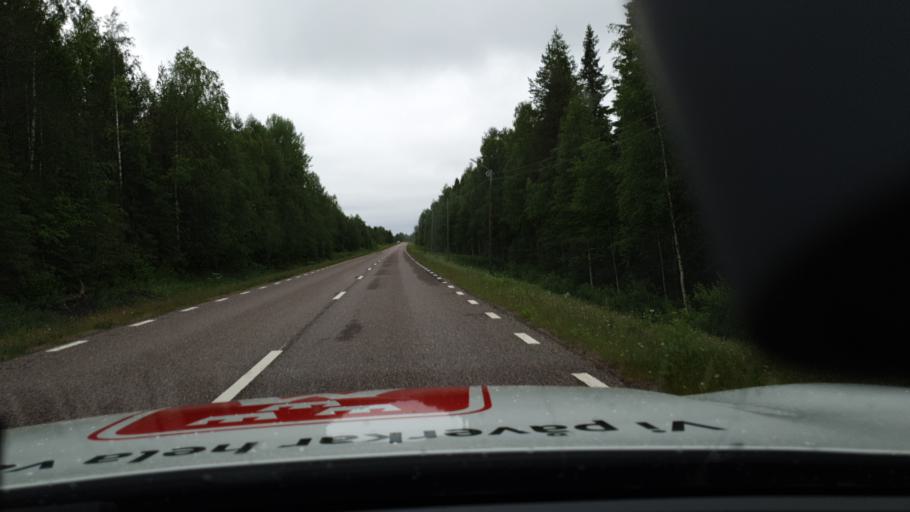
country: FI
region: Lapland
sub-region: Torniolaakso
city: Pello
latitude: 66.9333
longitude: 23.8506
